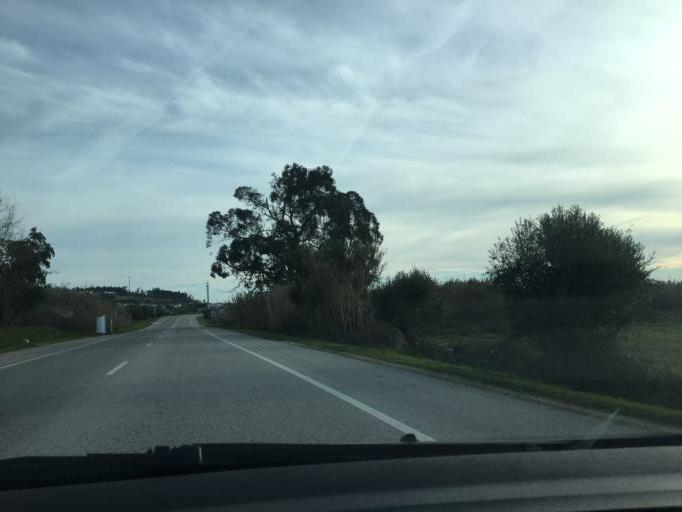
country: PT
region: Coimbra
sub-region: Soure
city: Alfarelos
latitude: 40.2043
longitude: -8.6337
